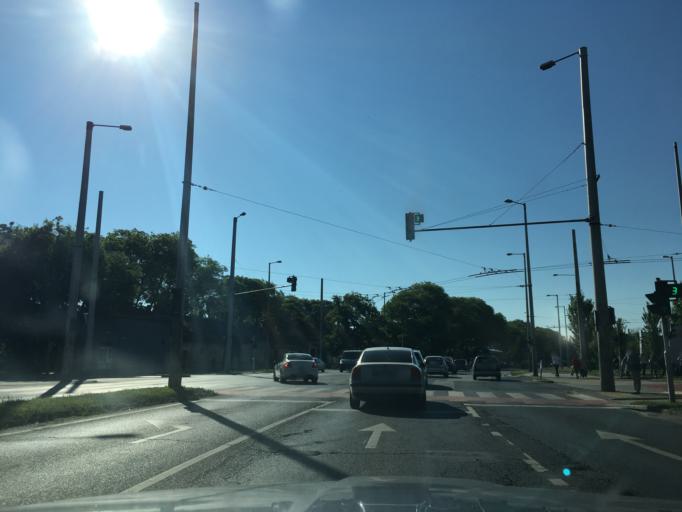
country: HU
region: Hajdu-Bihar
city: Debrecen
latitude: 47.5293
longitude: 21.6128
